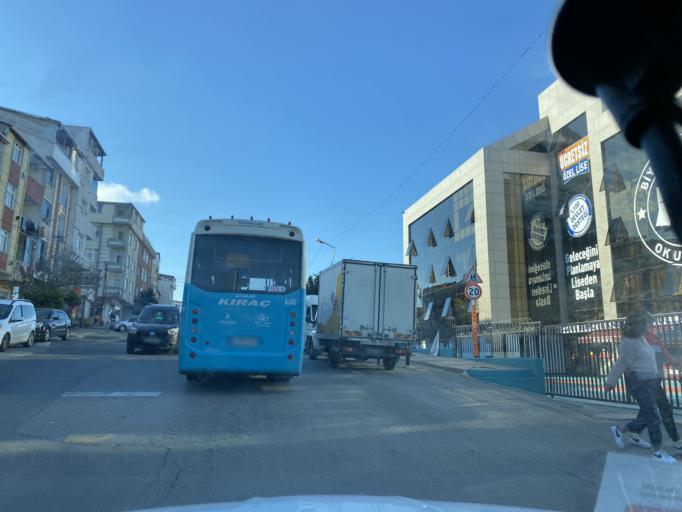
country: TR
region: Istanbul
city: Esenyurt
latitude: 41.0470
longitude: 28.6484
